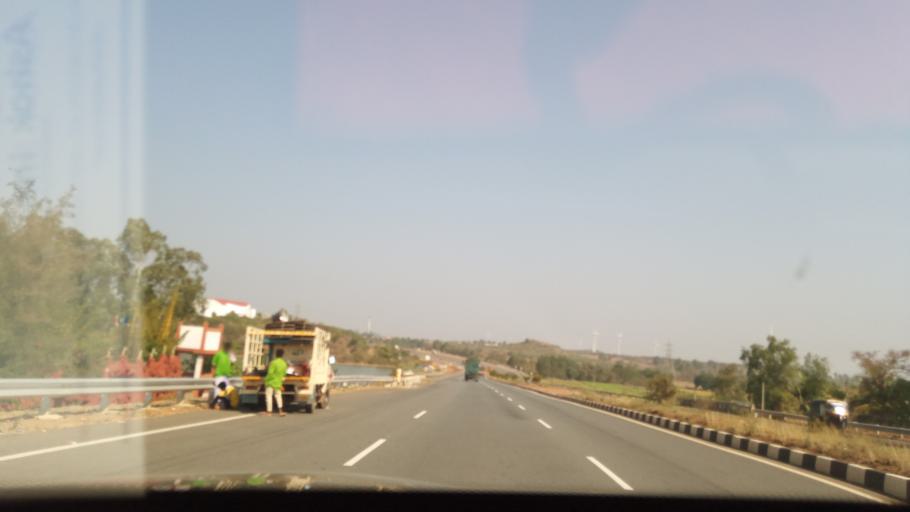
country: IN
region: Karnataka
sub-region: Haveri
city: Shiggaon
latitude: 15.0262
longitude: 75.1814
